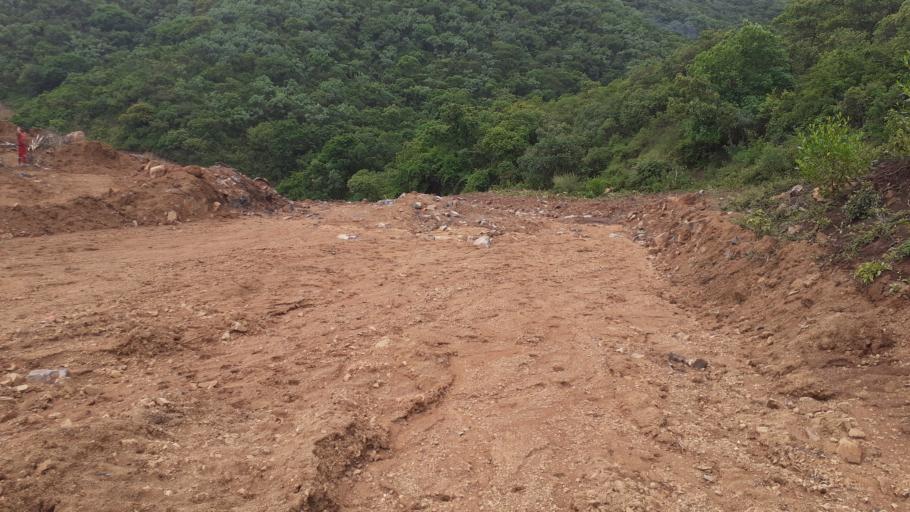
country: ET
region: Southern Nations, Nationalities, and People's Region
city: Areka
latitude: 7.5758
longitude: 37.5105
